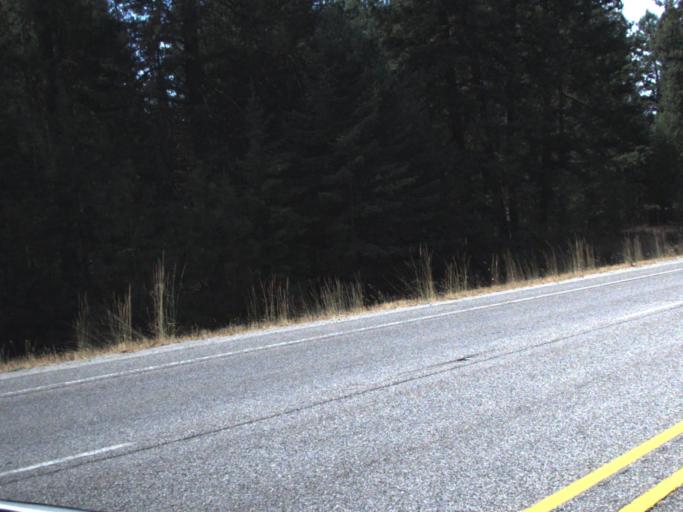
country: US
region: Washington
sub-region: Stevens County
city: Chewelah
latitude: 48.1470
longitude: -117.6840
